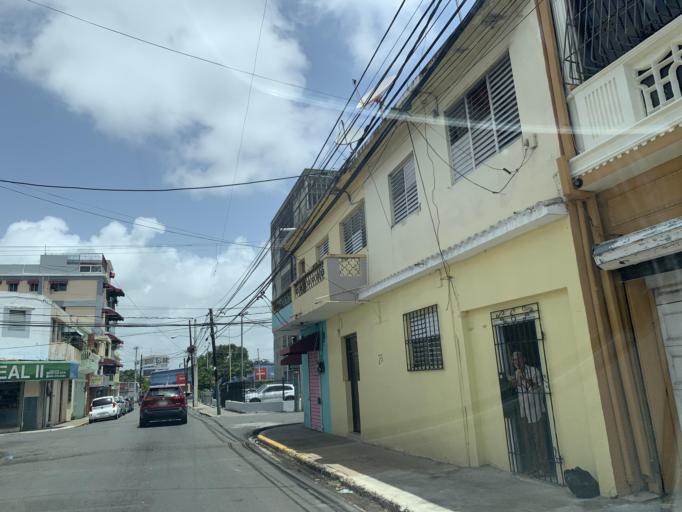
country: DO
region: Nacional
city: San Carlos
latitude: 18.4781
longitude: -69.9050
